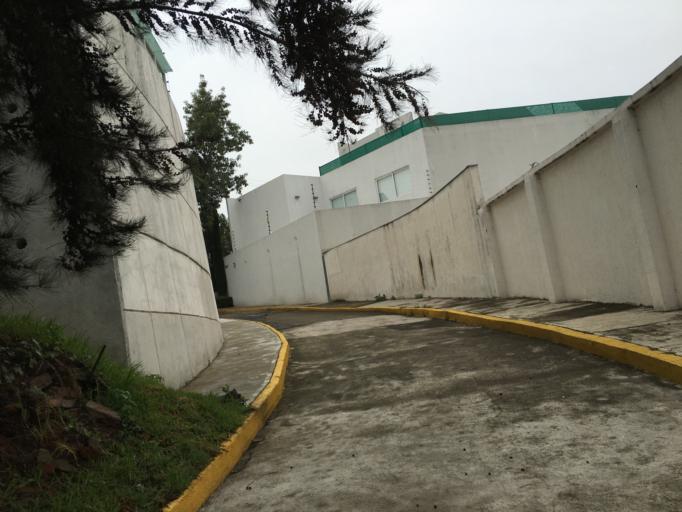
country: MX
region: Mexico City
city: Tlalpan
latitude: 19.2798
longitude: -99.1491
